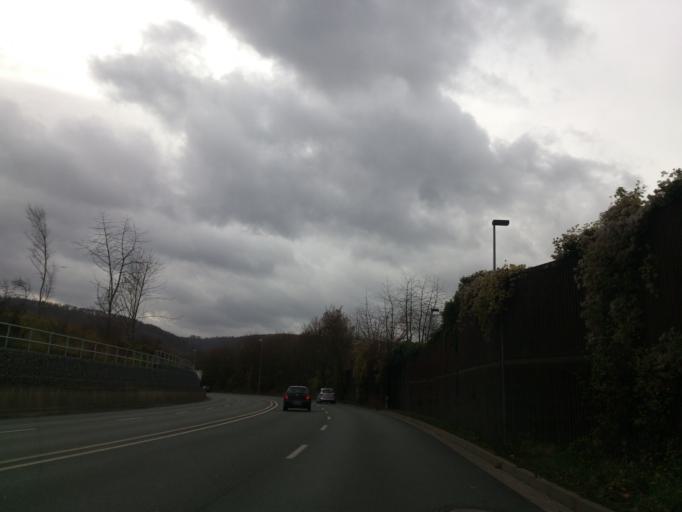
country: DE
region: North Rhine-Westphalia
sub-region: Regierungsbezirk Detmold
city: Hoexter
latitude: 51.7779
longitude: 9.3761
